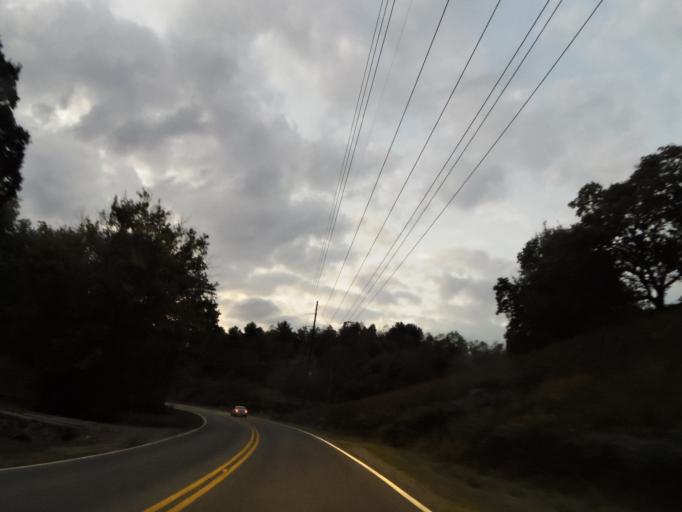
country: US
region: North Carolina
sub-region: Madison County
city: Marshall
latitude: 35.8302
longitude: -82.7042
